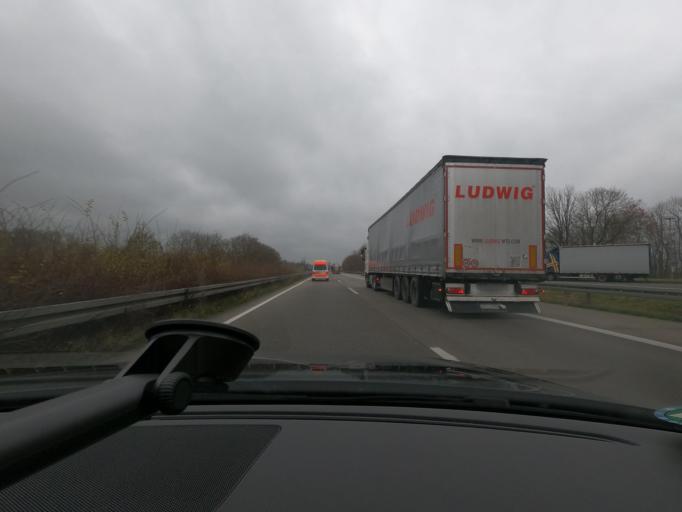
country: DE
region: North Rhine-Westphalia
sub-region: Regierungsbezirk Arnsberg
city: Soest
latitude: 51.5475
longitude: 8.1320
